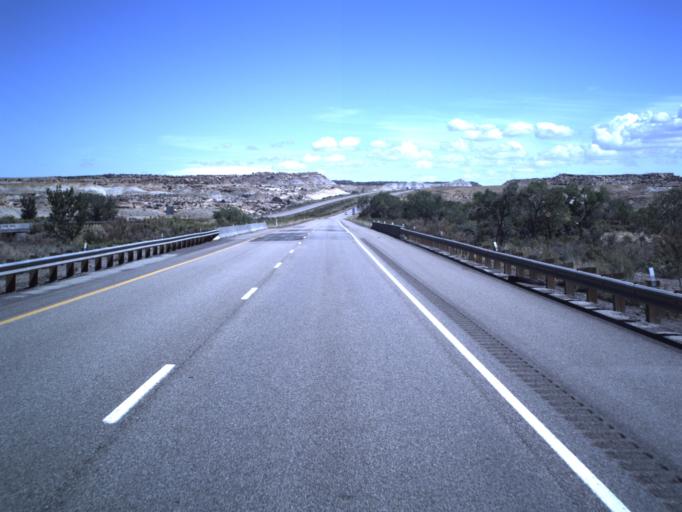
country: US
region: Utah
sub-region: Emery County
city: Ferron
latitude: 38.8127
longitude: -111.2015
